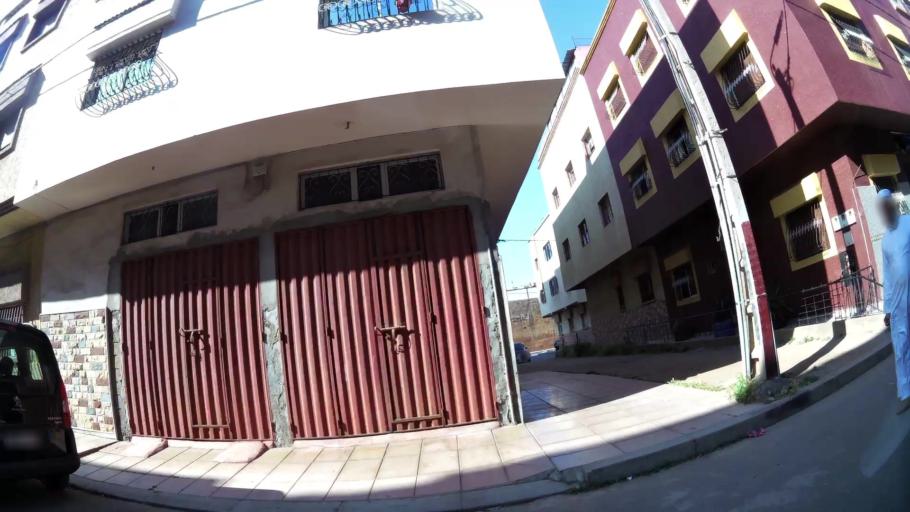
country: MA
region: Rabat-Sale-Zemmour-Zaer
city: Sale
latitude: 34.0467
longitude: -6.8153
